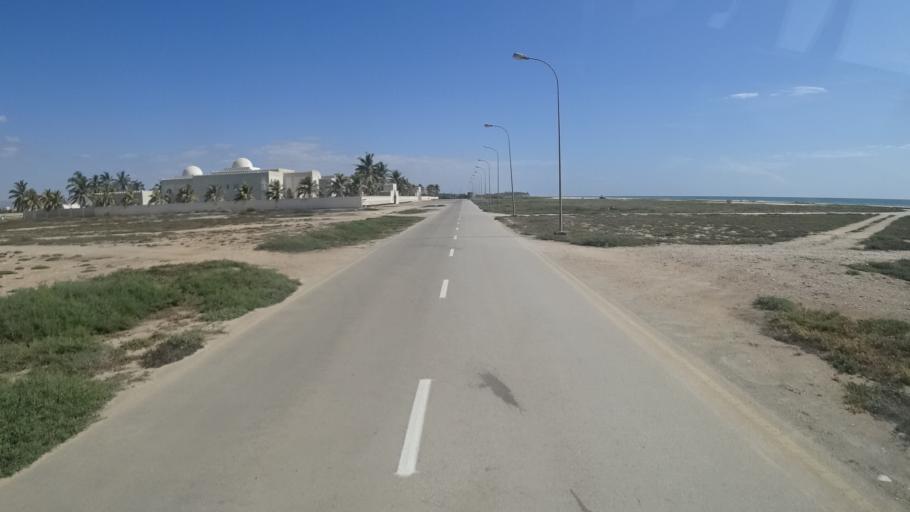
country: OM
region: Zufar
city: Salalah
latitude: 16.9943
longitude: 54.0608
